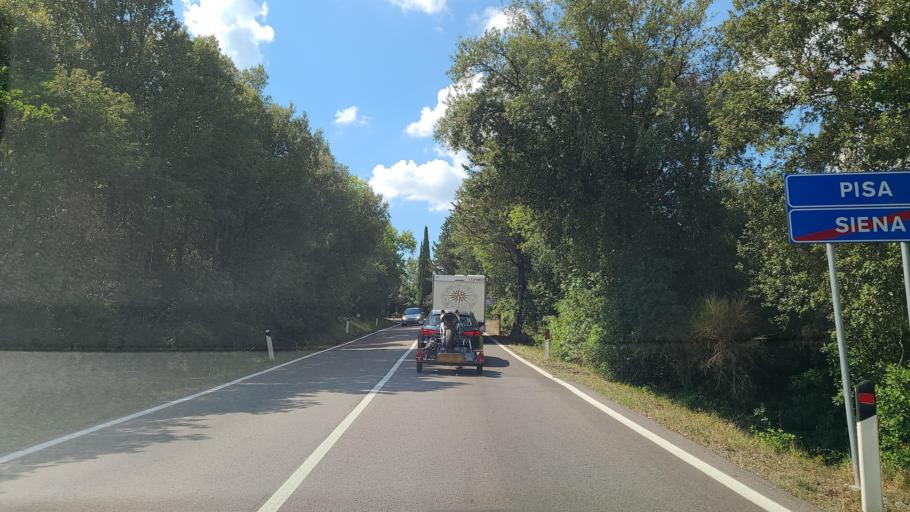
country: IT
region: Tuscany
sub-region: Provincia di Siena
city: San Gimignano
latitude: 43.4028
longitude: 11.0014
